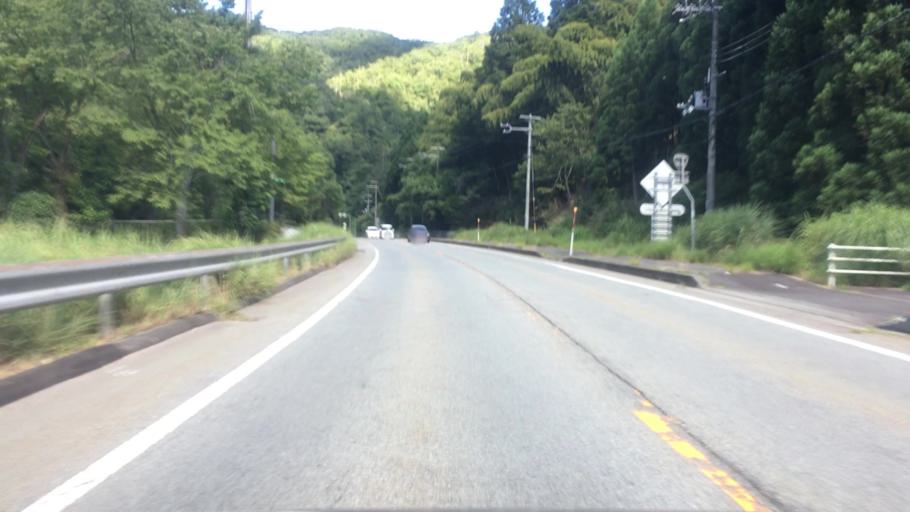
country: JP
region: Hyogo
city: Toyooka
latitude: 35.5774
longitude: 134.7528
